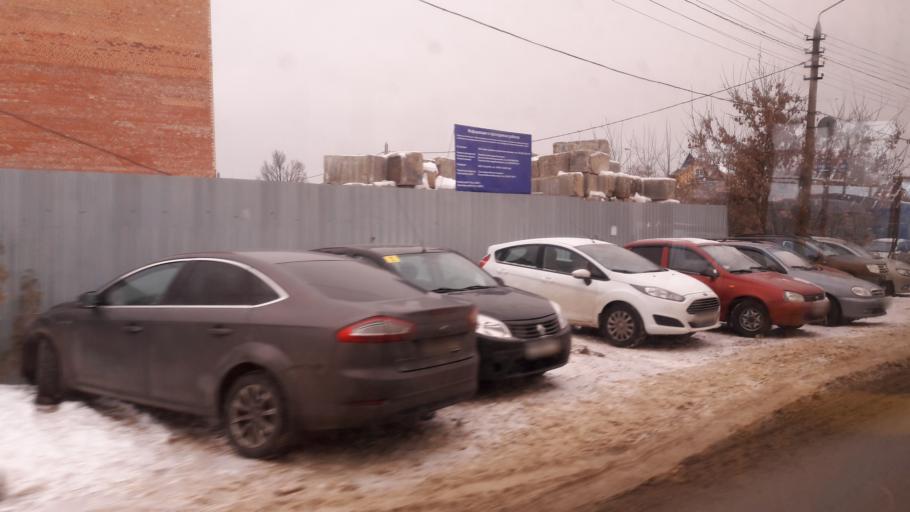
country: RU
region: Tula
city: Gorelki
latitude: 54.2340
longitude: 37.6259
